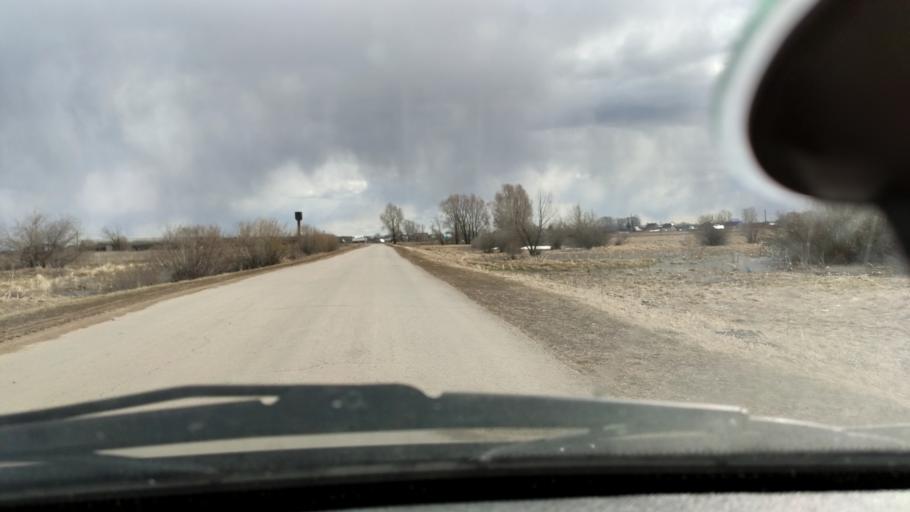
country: RU
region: Bashkortostan
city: Mikhaylovka
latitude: 54.9744
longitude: 55.7825
